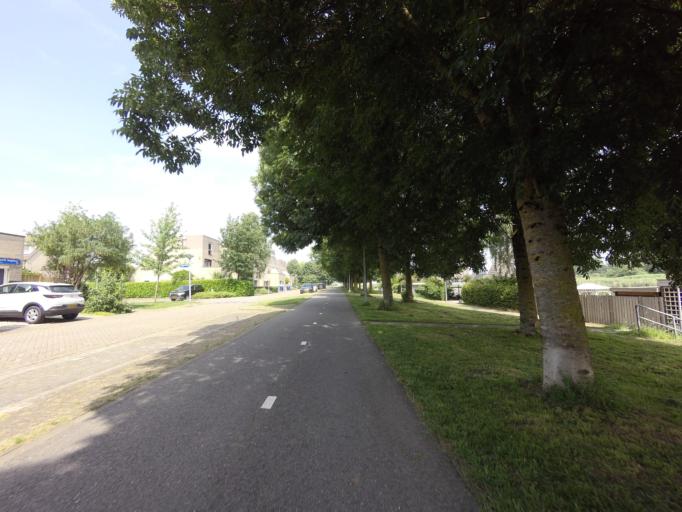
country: NL
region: Flevoland
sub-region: Gemeente Almere
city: Almere Stad
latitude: 52.3897
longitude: 5.2900
